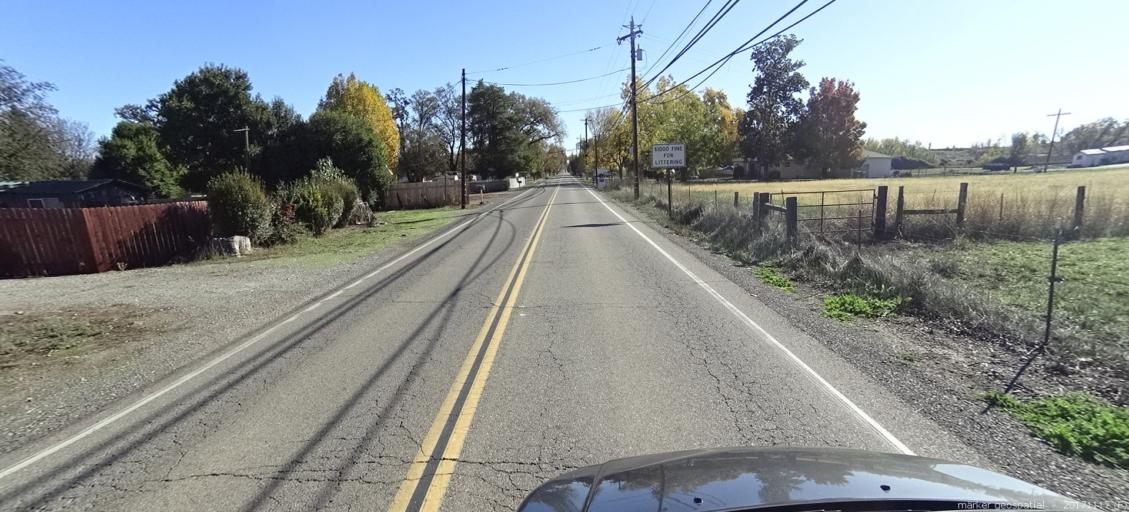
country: US
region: California
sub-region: Shasta County
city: Anderson
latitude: 40.4456
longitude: -122.2530
